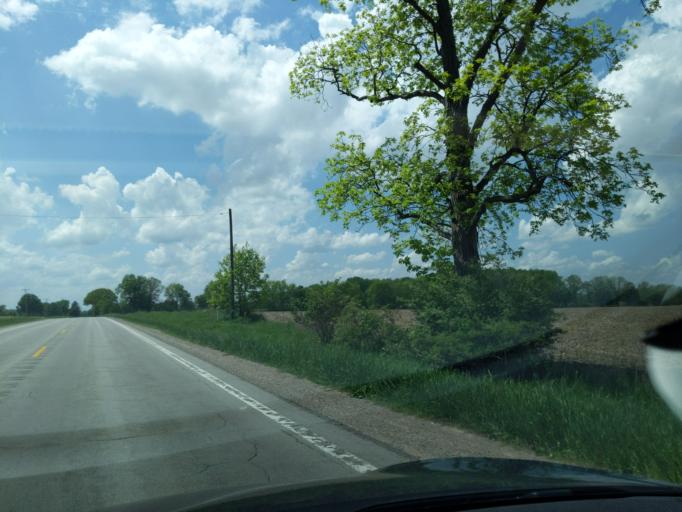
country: US
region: Michigan
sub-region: Ingham County
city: Stockbridge
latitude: 42.5560
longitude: -84.2473
